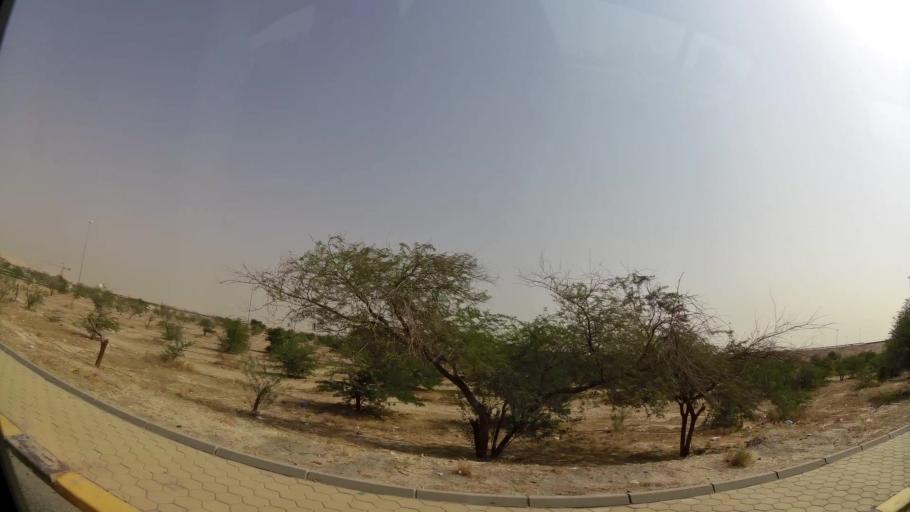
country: KW
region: Muhafazat al Jahra'
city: Al Jahra'
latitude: 29.3756
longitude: 47.6601
